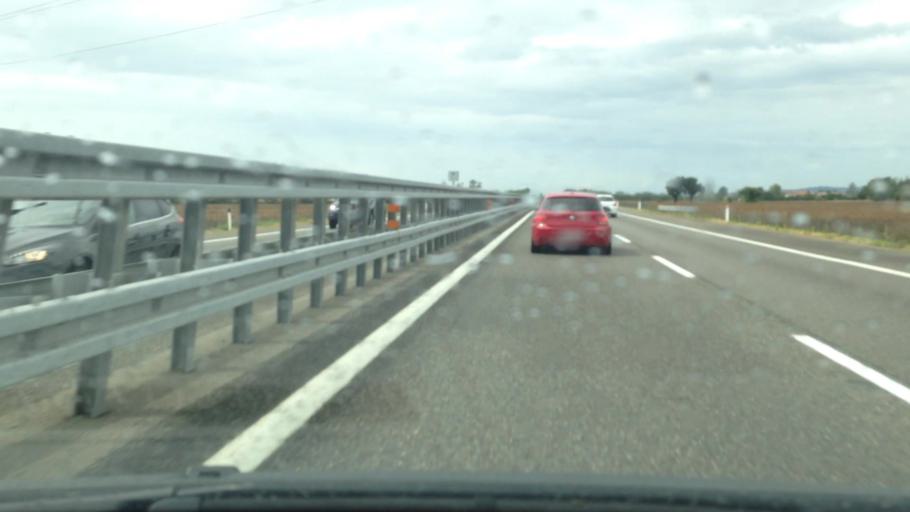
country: IT
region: Piedmont
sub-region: Provincia di Alessandria
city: San Giuliano Vecchio
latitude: 44.9163
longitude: 8.7925
